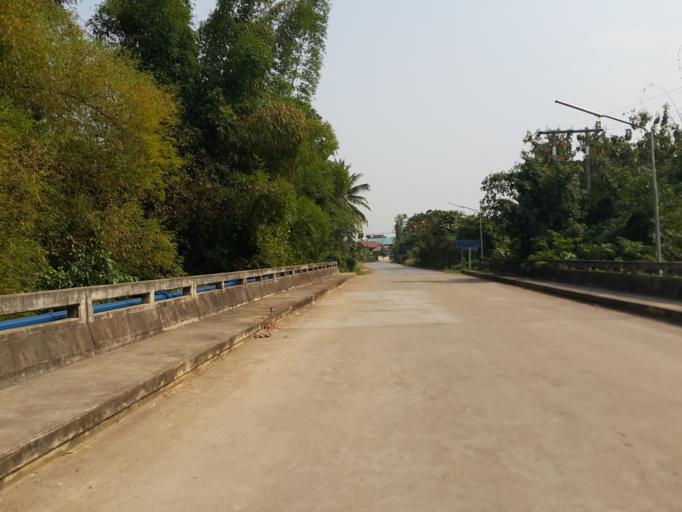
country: TH
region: Sukhothai
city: Thung Saliam
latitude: 17.3228
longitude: 99.5180
